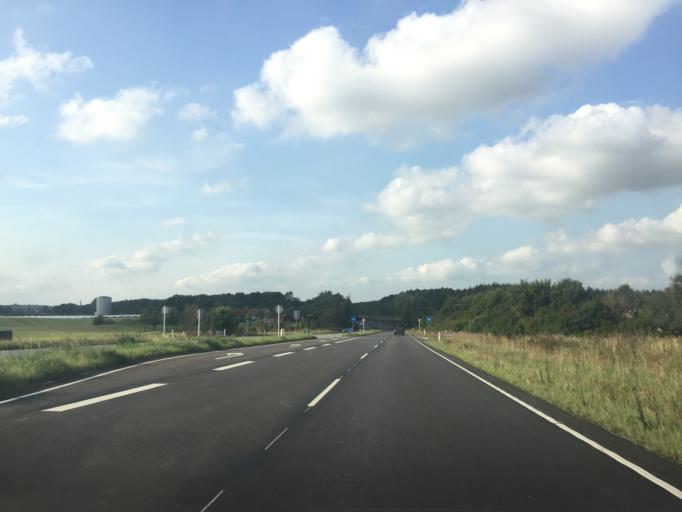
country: DK
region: Zealand
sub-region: Holbaek Kommune
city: Jyderup
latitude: 55.6540
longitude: 11.4298
